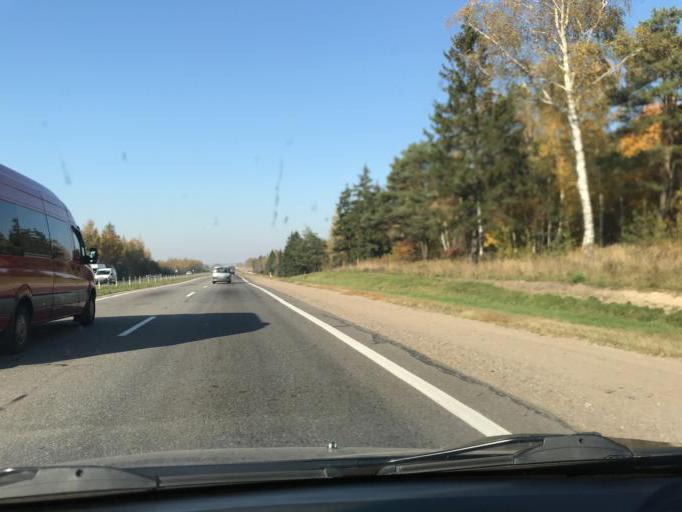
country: BY
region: Minsk
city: Luhavaya Slabada
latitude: 53.7144
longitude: 27.8694
